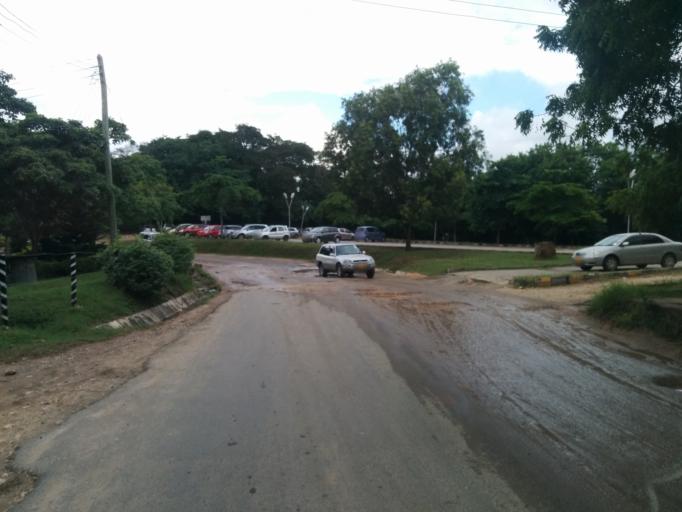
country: TZ
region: Dar es Salaam
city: Magomeni
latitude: -6.7804
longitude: 39.2010
